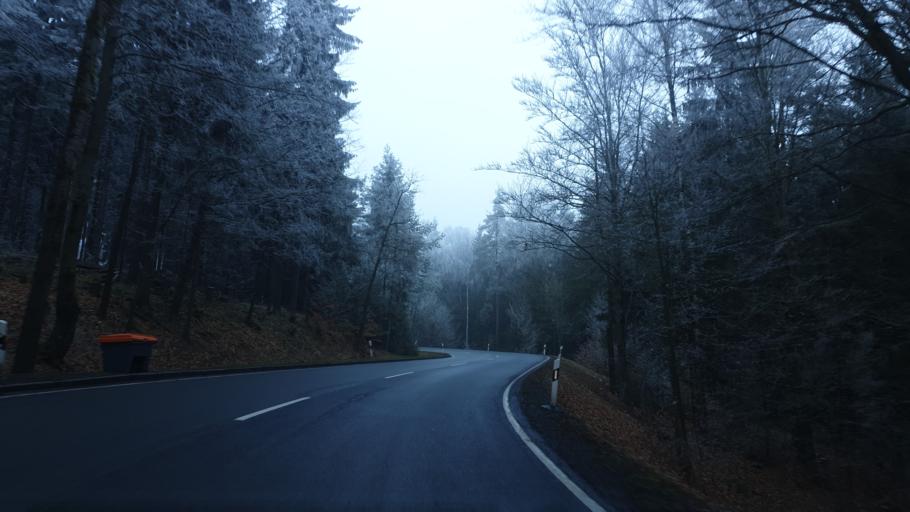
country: DE
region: Saxony
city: Bad Brambach
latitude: 50.1925
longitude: 12.3146
